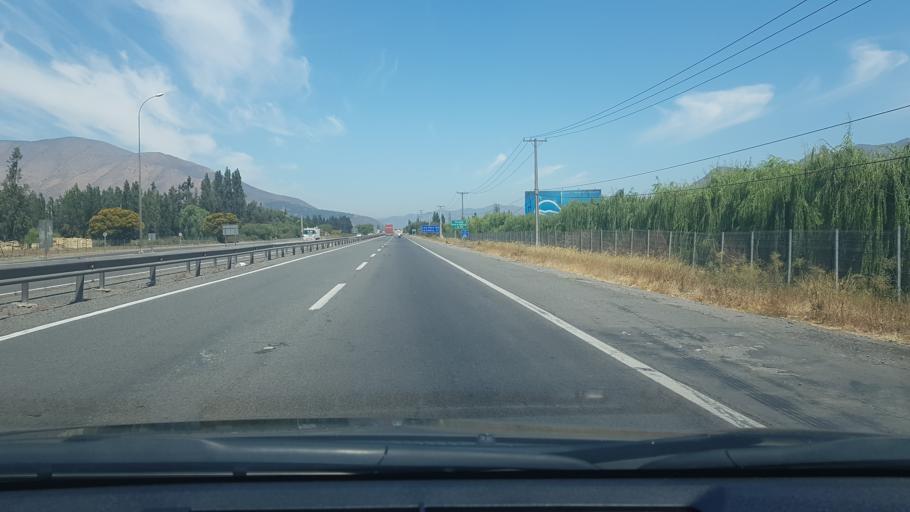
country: CL
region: Valparaiso
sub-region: Provincia de San Felipe
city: Llaillay
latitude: -32.8503
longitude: -70.9472
